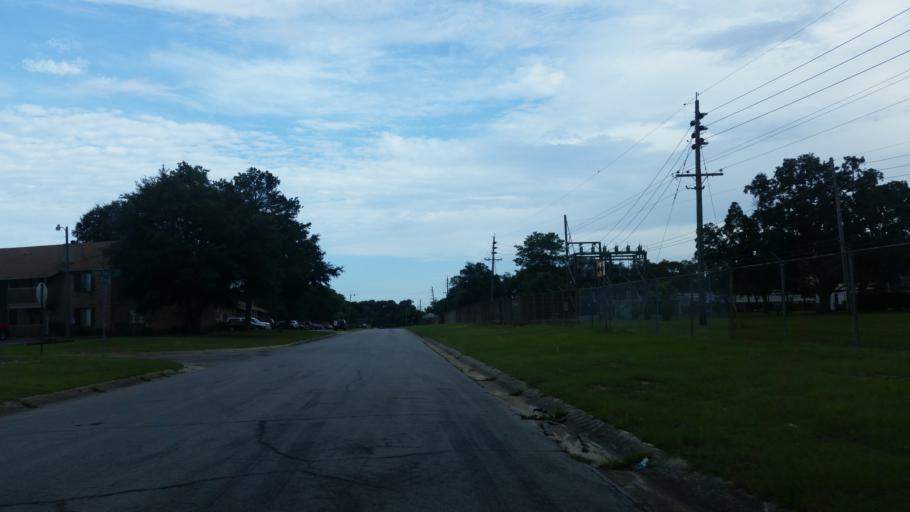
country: US
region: Florida
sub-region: Escambia County
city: West Pensacola
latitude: 30.4094
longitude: -87.2815
